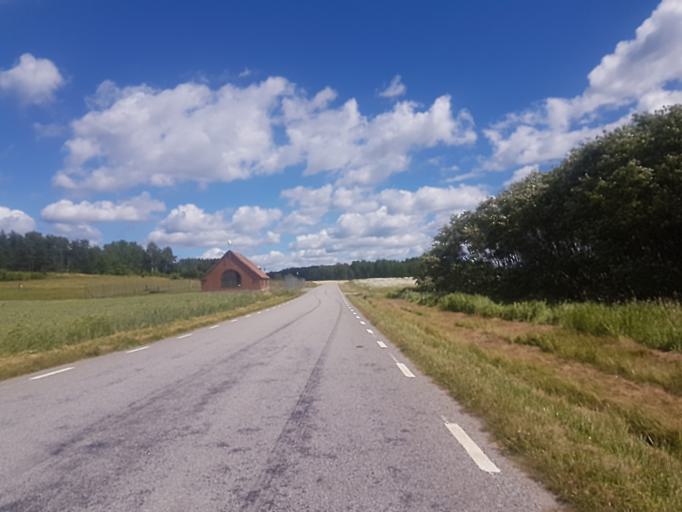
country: SE
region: Soedermanland
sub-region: Gnesta Kommun
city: Gnesta
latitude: 59.0445
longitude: 17.3302
